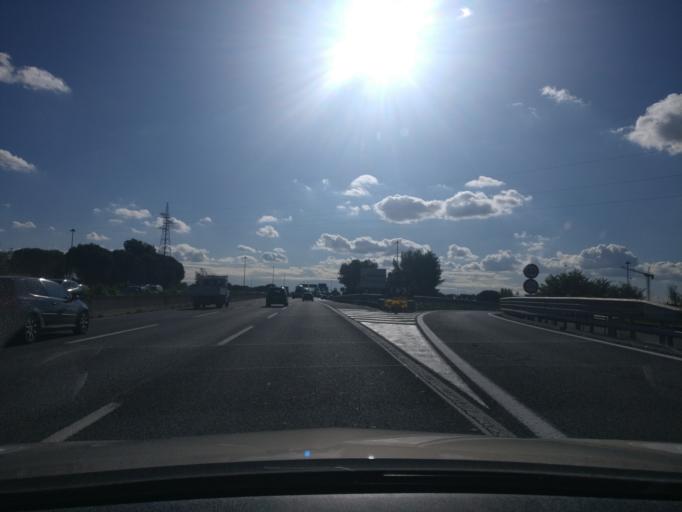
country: IT
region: Latium
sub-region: Citta metropolitana di Roma Capitale
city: Ciampino
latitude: 41.8418
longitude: 12.5924
